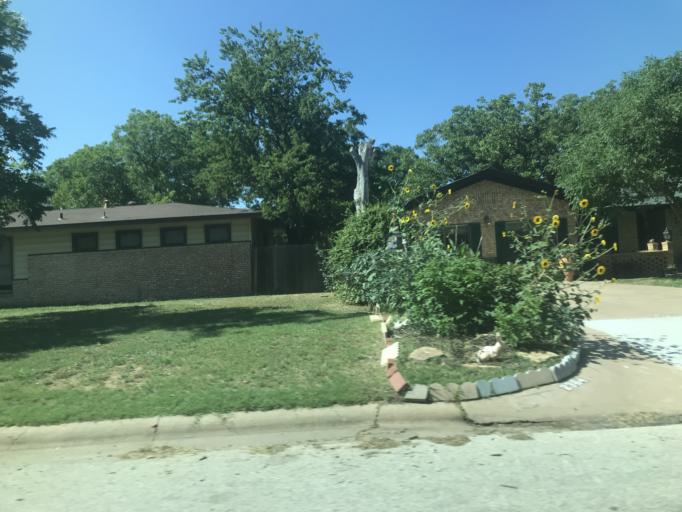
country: US
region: Texas
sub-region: Taylor County
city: Abilene
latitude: 32.4097
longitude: -99.7528
